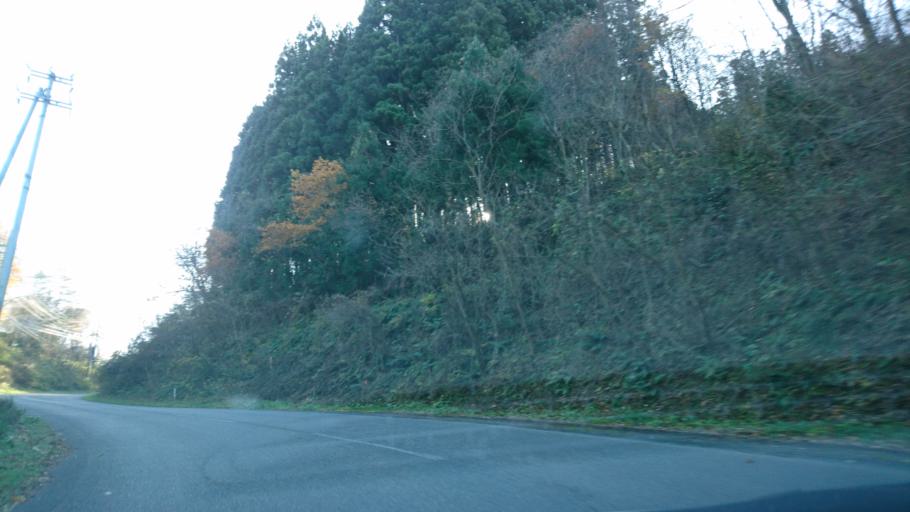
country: JP
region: Iwate
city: Ichinoseki
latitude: 38.8619
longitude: 141.3397
